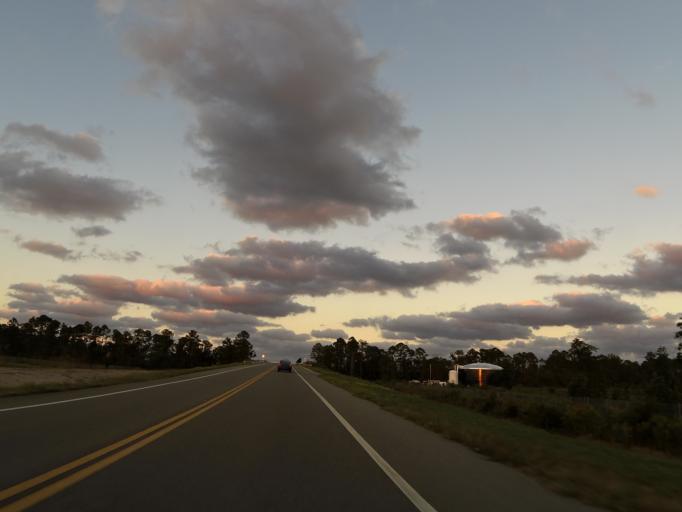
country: US
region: Florida
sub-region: Saint Johns County
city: Palm Valley
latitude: 30.0883
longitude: -81.4667
